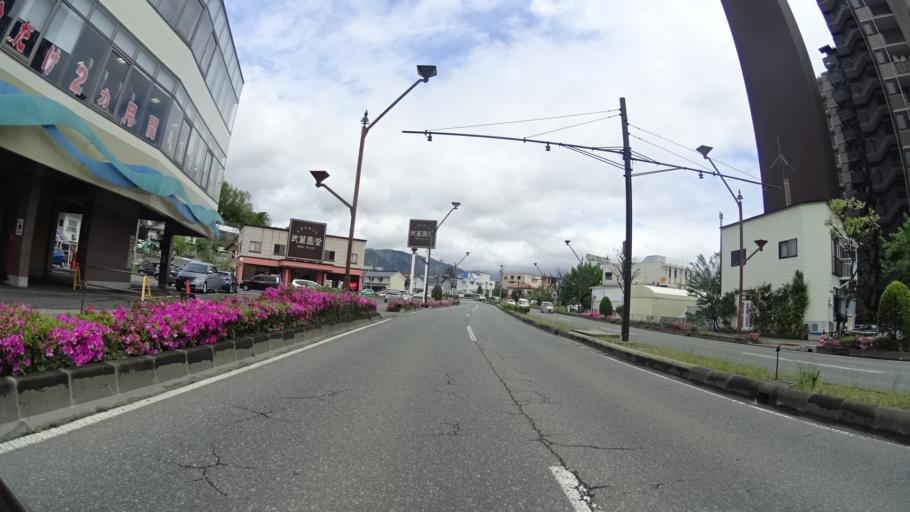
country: JP
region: Nagano
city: Nagano-shi
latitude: 36.6594
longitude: 138.1937
